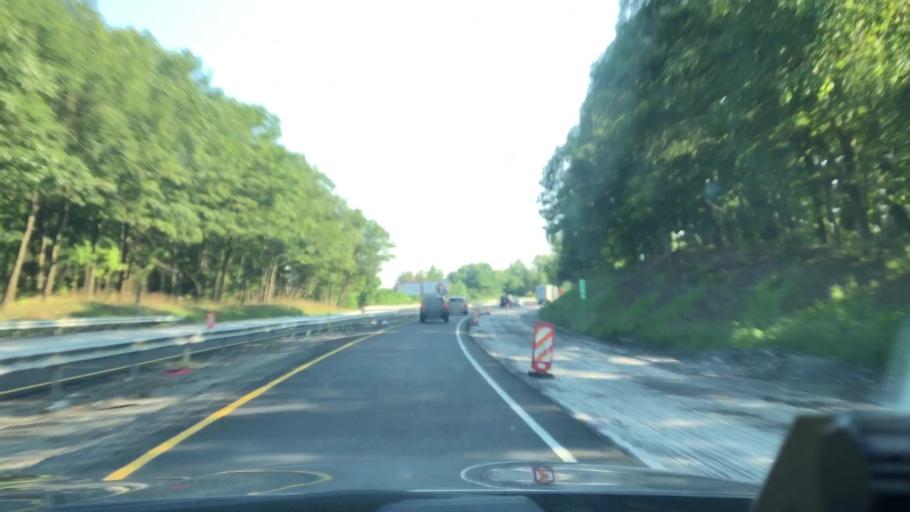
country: US
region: Pennsylvania
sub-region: Monroe County
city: Arlington Heights
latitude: 40.9733
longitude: -75.2756
